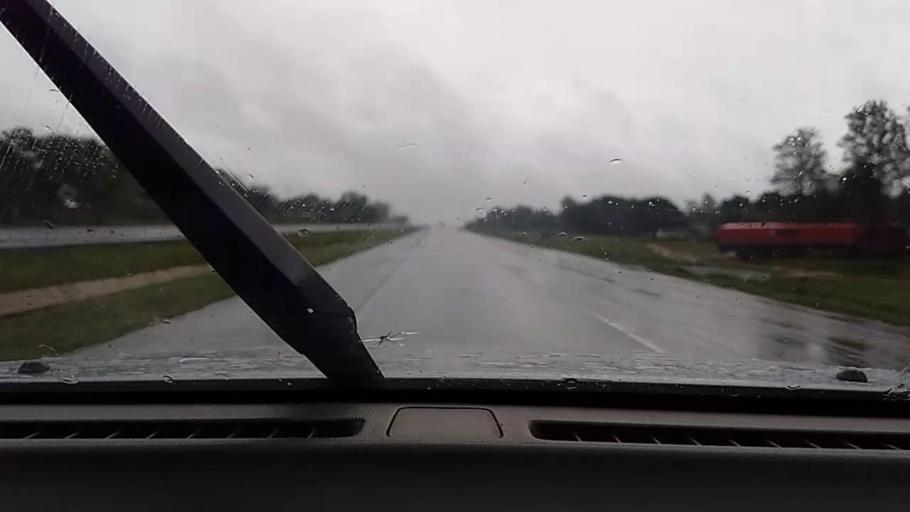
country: PY
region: Caaguazu
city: Repatriacion
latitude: -25.4663
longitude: -55.9380
